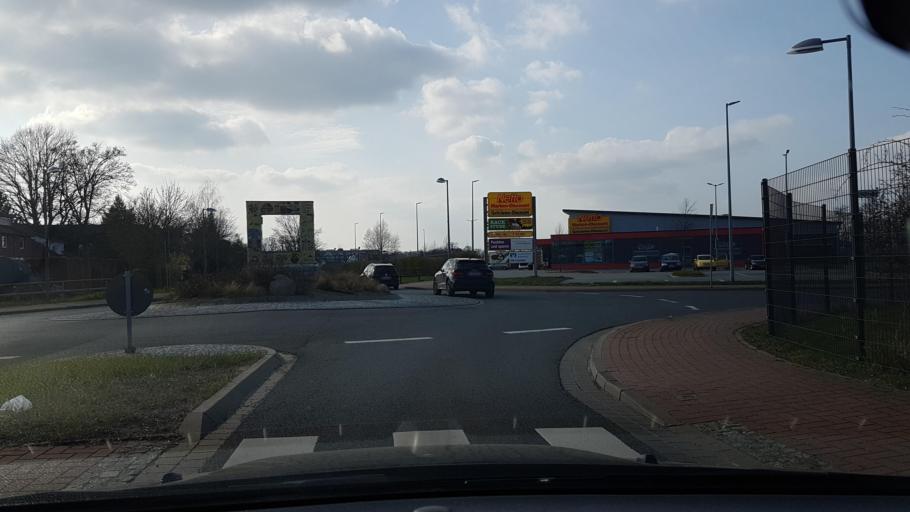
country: DE
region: Lower Saxony
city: Garbsen-Mitte
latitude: 52.4403
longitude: 9.5827
